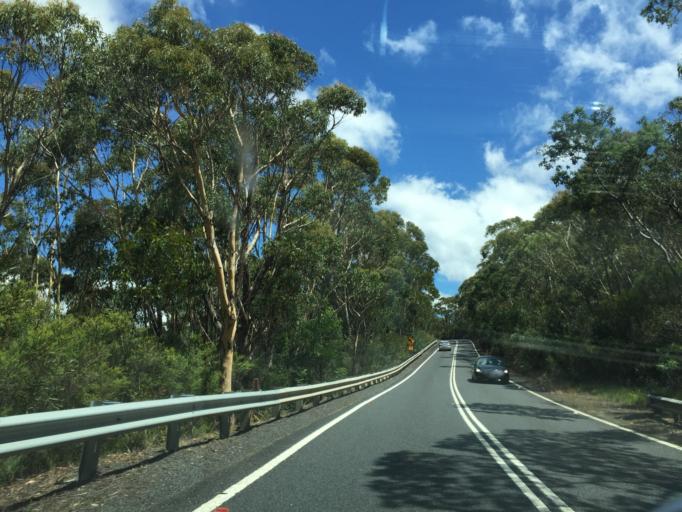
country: AU
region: New South Wales
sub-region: Blue Mountains Municipality
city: Blackheath
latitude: -33.5647
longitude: 150.3656
